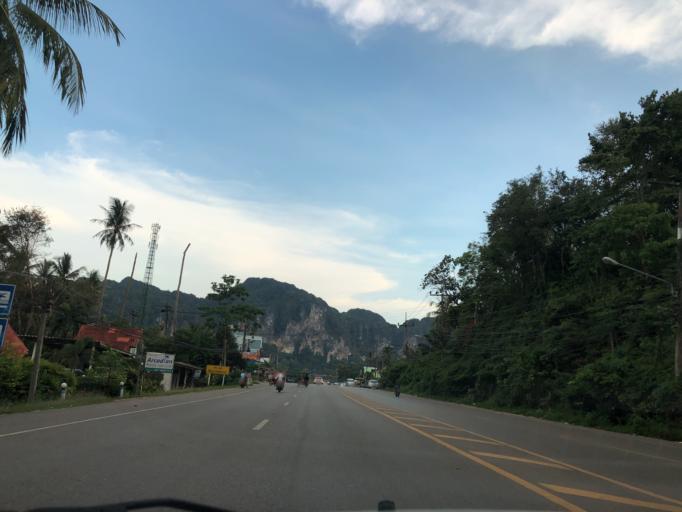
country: TH
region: Phangnga
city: Ban Ao Nang
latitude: 8.0454
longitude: 98.8374
